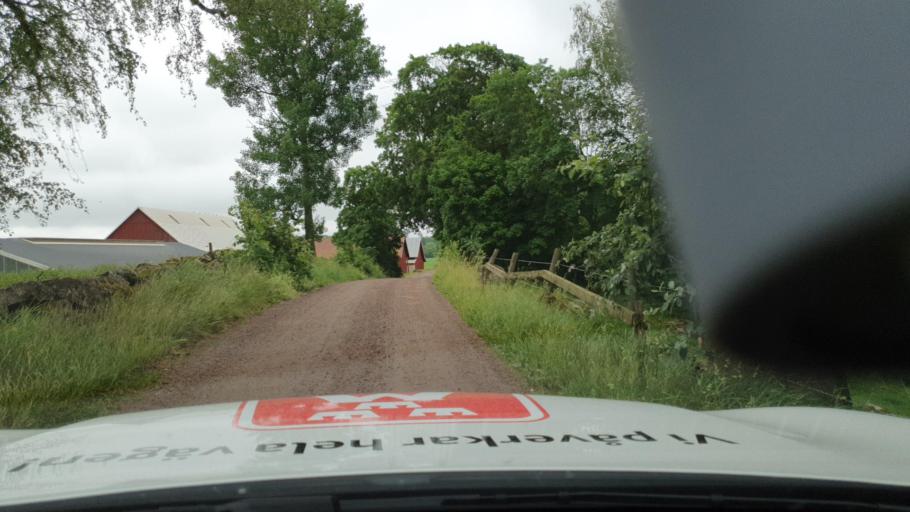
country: SE
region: Vaestra Goetaland
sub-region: Skovde Kommun
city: Stopen
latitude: 58.4003
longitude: 13.9962
